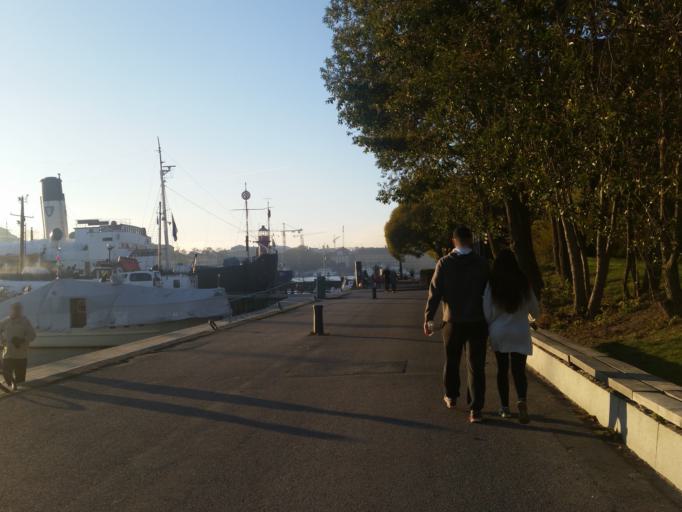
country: SE
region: Stockholm
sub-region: Stockholms Kommun
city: OEstermalm
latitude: 59.3272
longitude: 18.0928
